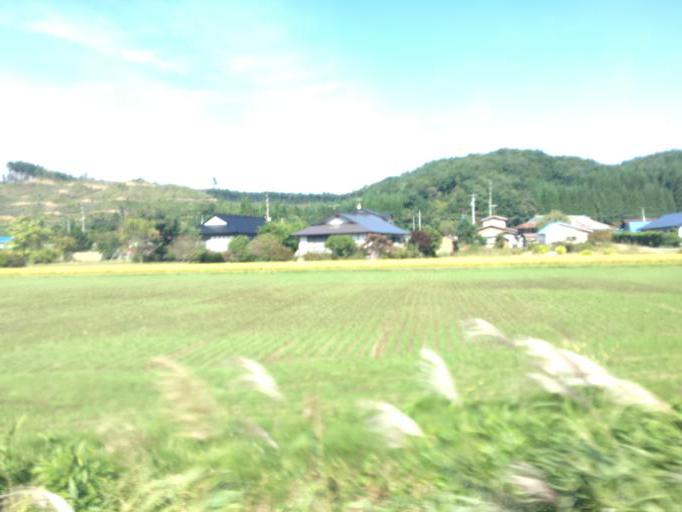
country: JP
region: Iwate
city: Shizukuishi
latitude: 39.9705
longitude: 141.0396
